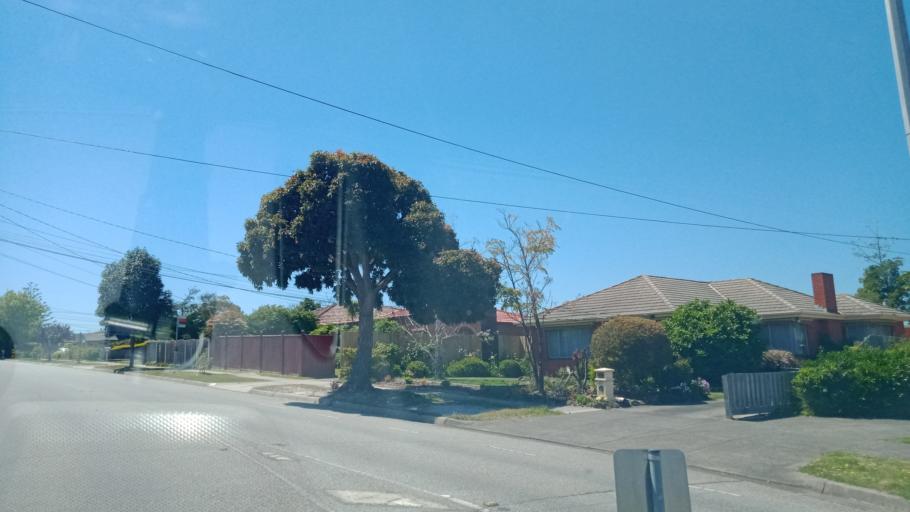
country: AU
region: Victoria
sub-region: Greater Dandenong
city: Springvale
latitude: -37.9305
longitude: 145.1725
